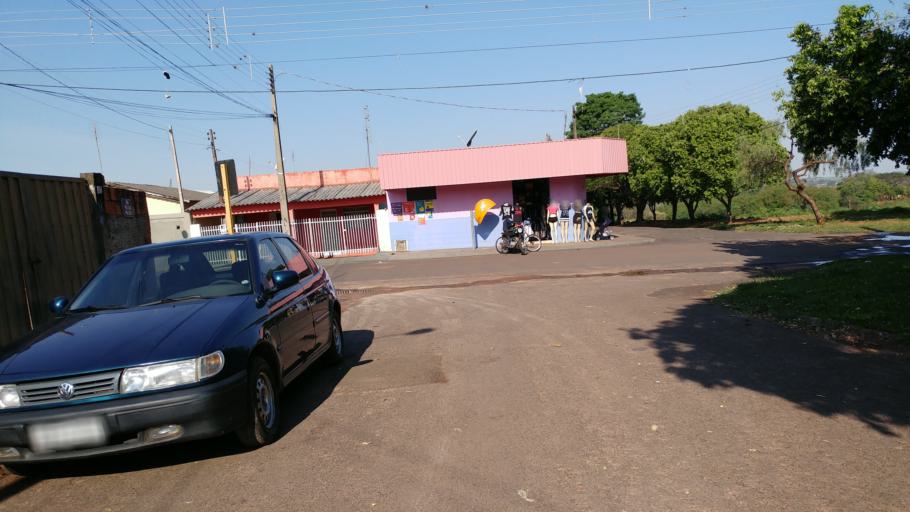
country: BR
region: Sao Paulo
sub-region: Paraguacu Paulista
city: Paraguacu Paulista
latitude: -22.4188
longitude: -50.5683
